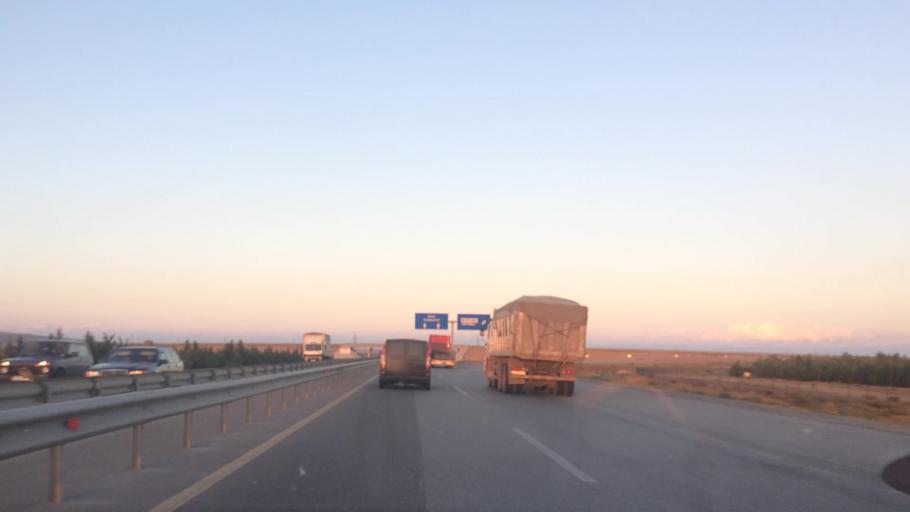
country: AZ
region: Baki
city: Qobustan
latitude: 39.9519
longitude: 49.3734
